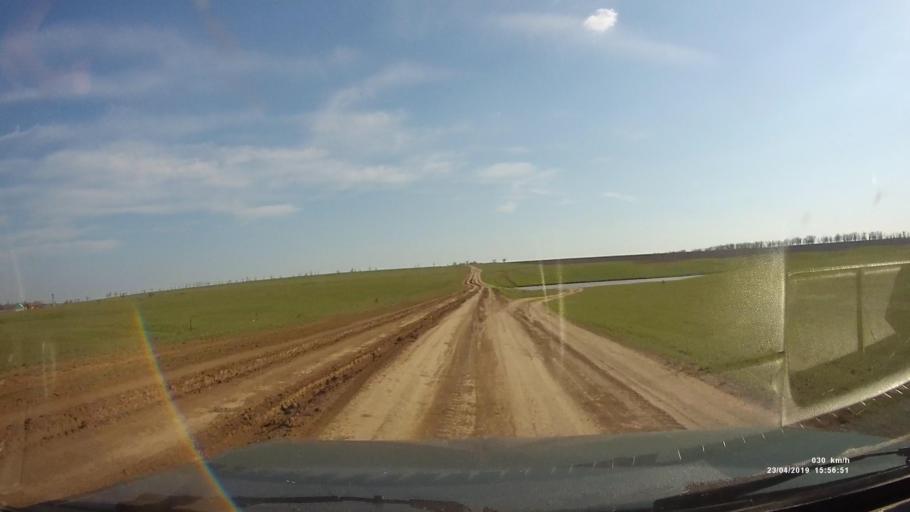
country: RU
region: Rostov
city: Remontnoye
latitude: 46.5350
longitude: 43.1107
